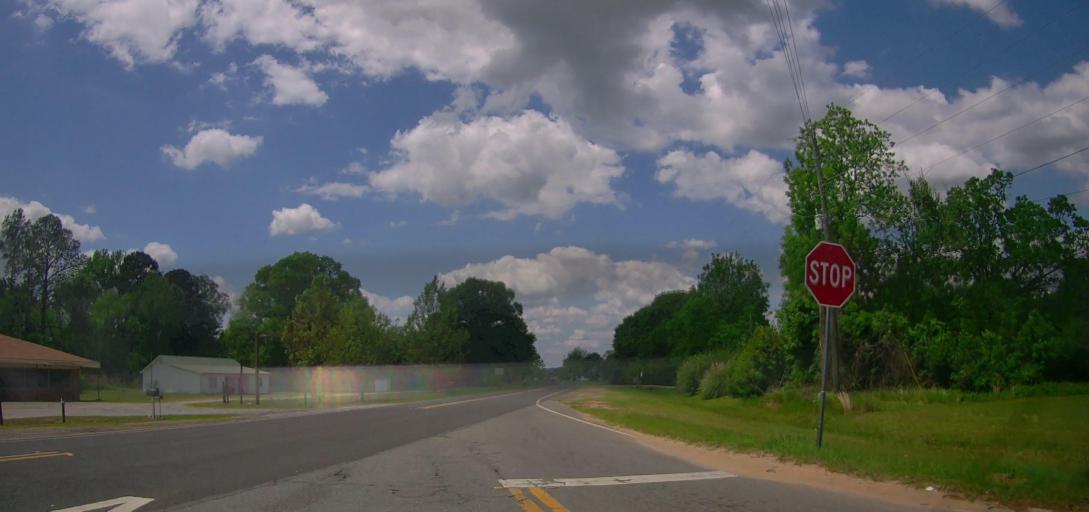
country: US
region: Georgia
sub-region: Laurens County
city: East Dublin
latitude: 32.5221
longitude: -82.8058
